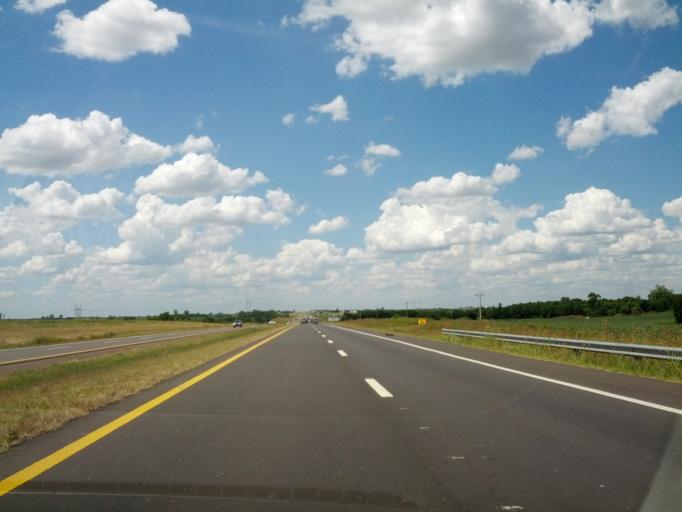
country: AR
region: Entre Rios
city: Colonia Elia
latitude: -32.5757
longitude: -58.3850
